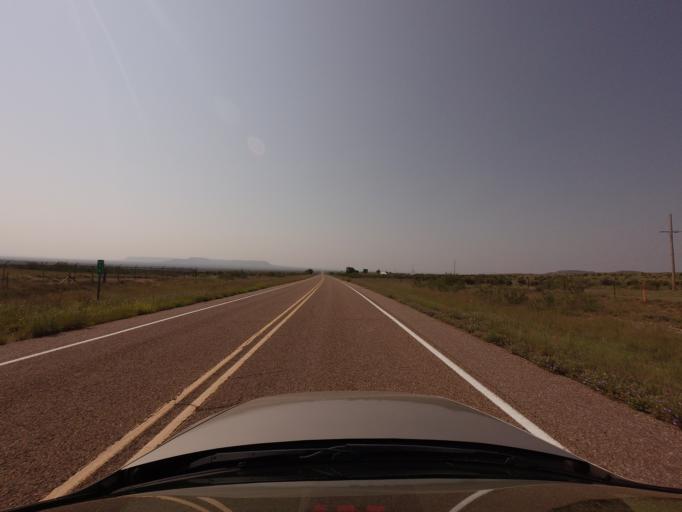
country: US
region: New Mexico
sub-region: Quay County
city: Tucumcari
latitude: 35.0960
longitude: -103.7375
